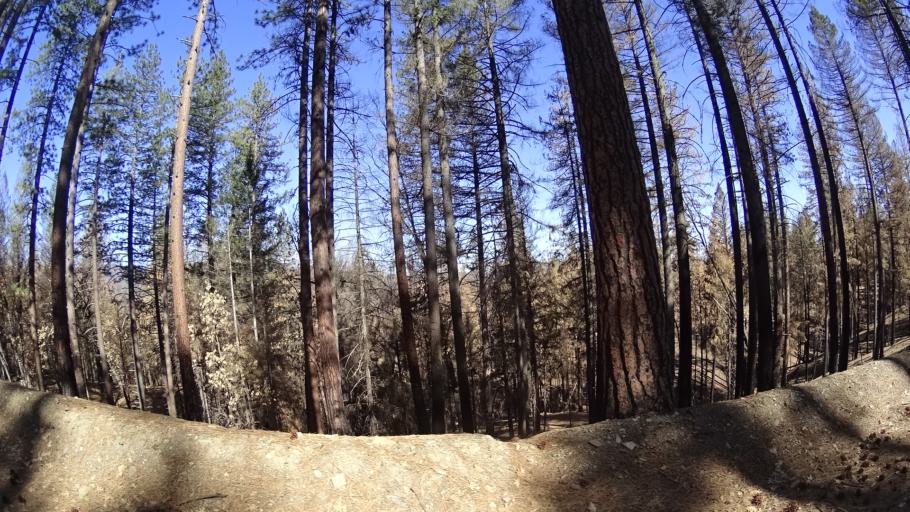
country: US
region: California
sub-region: Tehama County
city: Rancho Tehama Reserve
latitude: 39.6572
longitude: -122.7193
